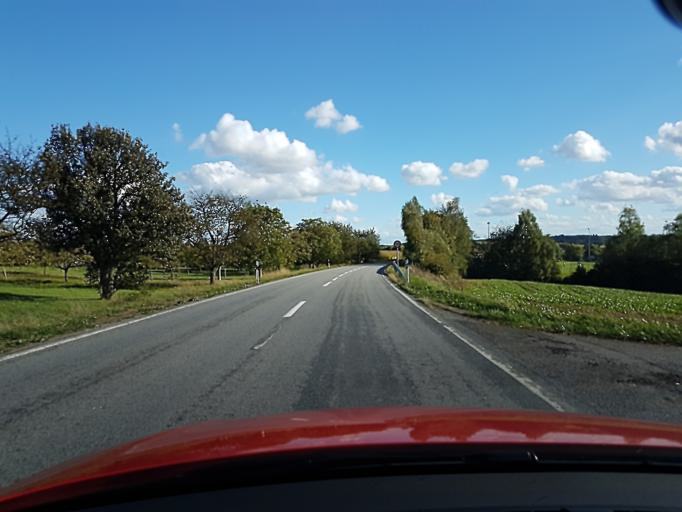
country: DE
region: Baden-Wuerttemberg
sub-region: Karlsruhe Region
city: Spechbach
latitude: 49.3520
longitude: 8.8791
